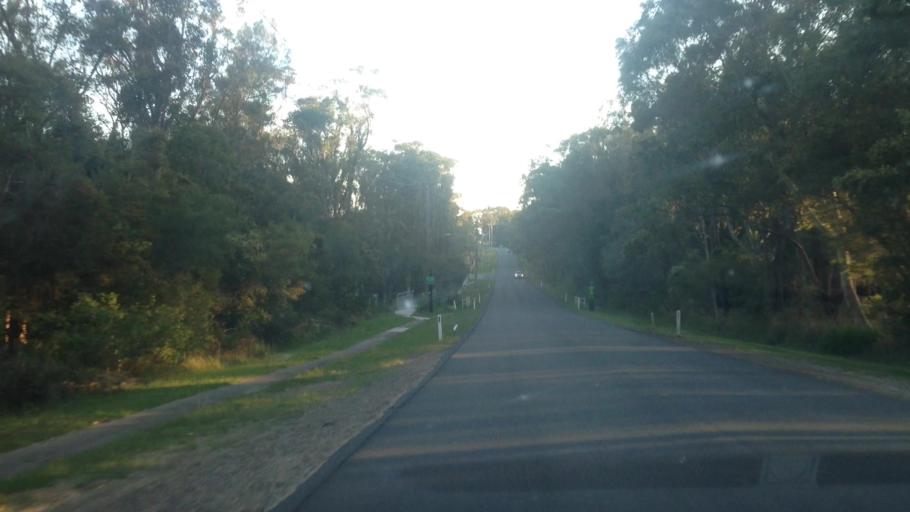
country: AU
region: New South Wales
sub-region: Wyong Shire
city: Kingfisher Shores
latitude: -33.1489
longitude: 151.5194
